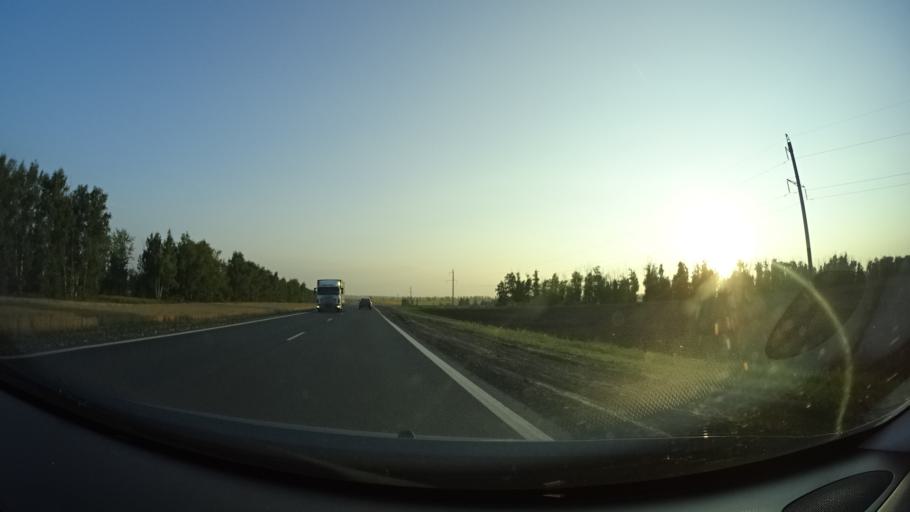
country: RU
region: Samara
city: Sernovodsk
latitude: 53.9563
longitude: 51.3957
